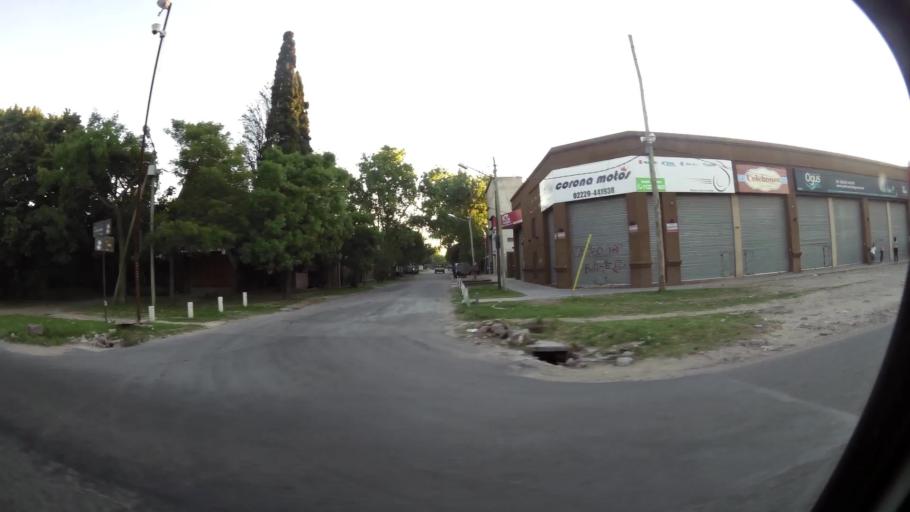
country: AR
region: Buenos Aires
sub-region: Partido de Quilmes
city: Quilmes
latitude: -34.8204
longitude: -58.1924
